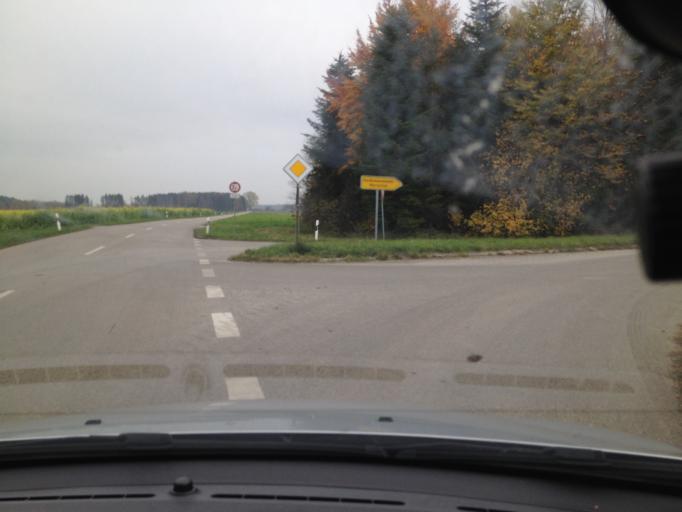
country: DE
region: Bavaria
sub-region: Swabia
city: Amberg
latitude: 48.0991
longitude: 10.7003
